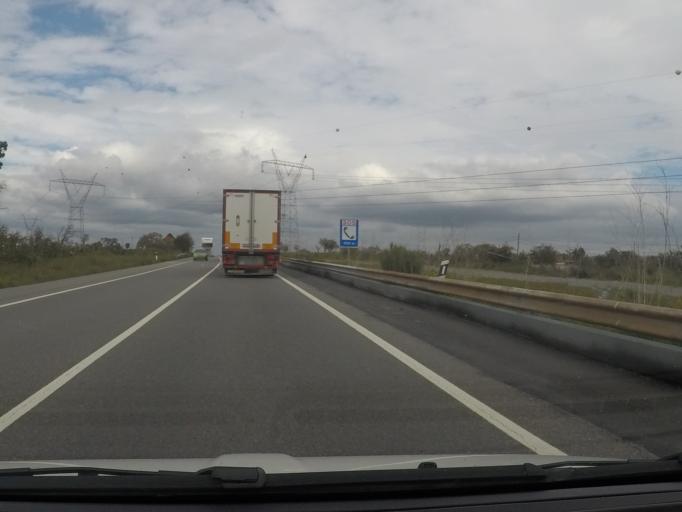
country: PT
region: Setubal
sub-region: Santiago do Cacem
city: Santiago do Cacem
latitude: 38.0714
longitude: -8.6560
